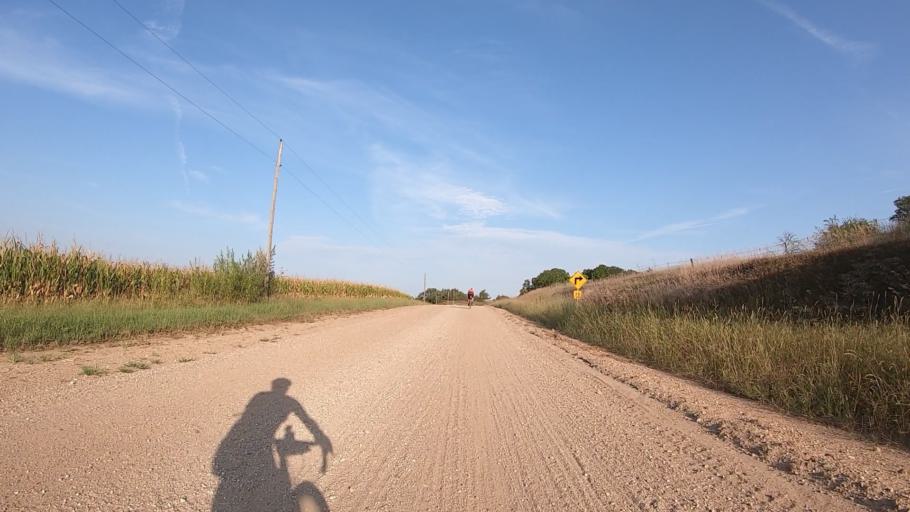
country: US
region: Kansas
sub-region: Marshall County
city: Blue Rapids
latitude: 39.7250
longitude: -96.7855
